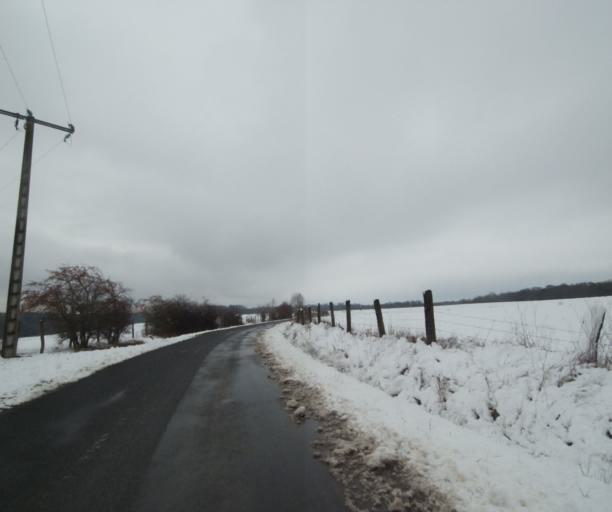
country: FR
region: Champagne-Ardenne
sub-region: Departement de la Haute-Marne
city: Laneuville-a-Remy
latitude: 48.4771
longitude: 4.8815
